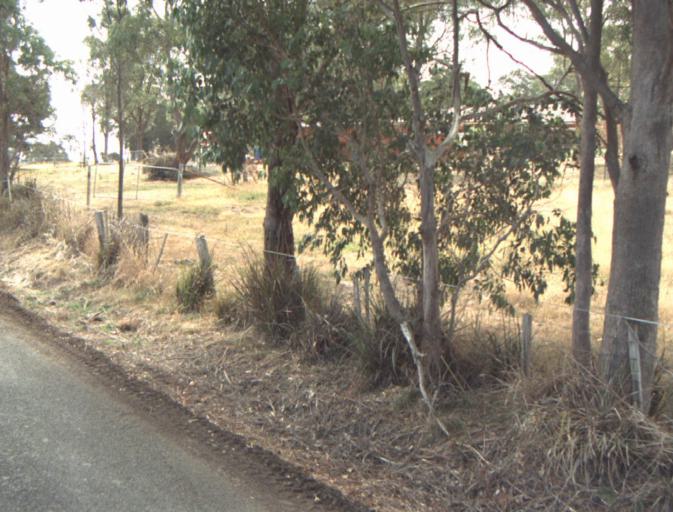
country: AU
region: Tasmania
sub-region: Launceston
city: Mayfield
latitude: -41.3042
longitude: 147.0377
